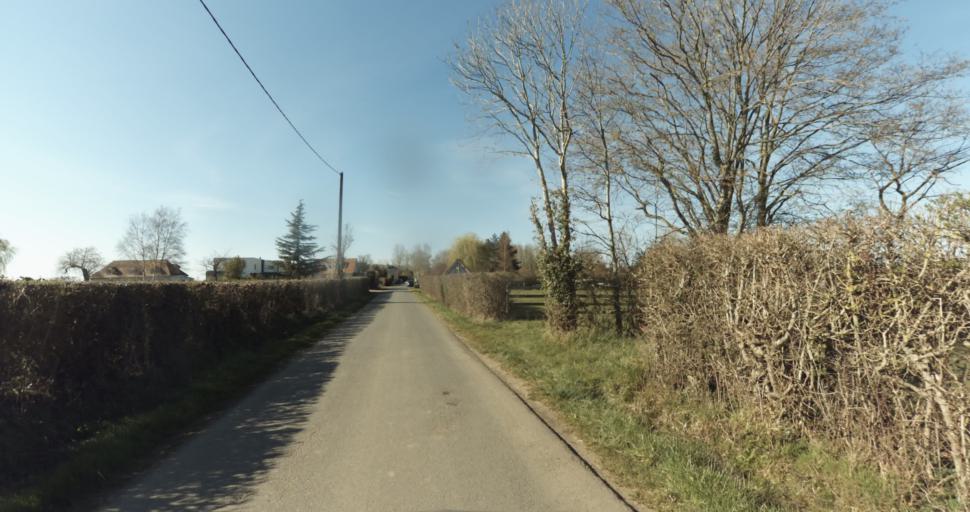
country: FR
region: Lower Normandy
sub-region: Departement du Calvados
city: Saint-Pierre-sur-Dives
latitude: 49.0345
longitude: 0.0536
